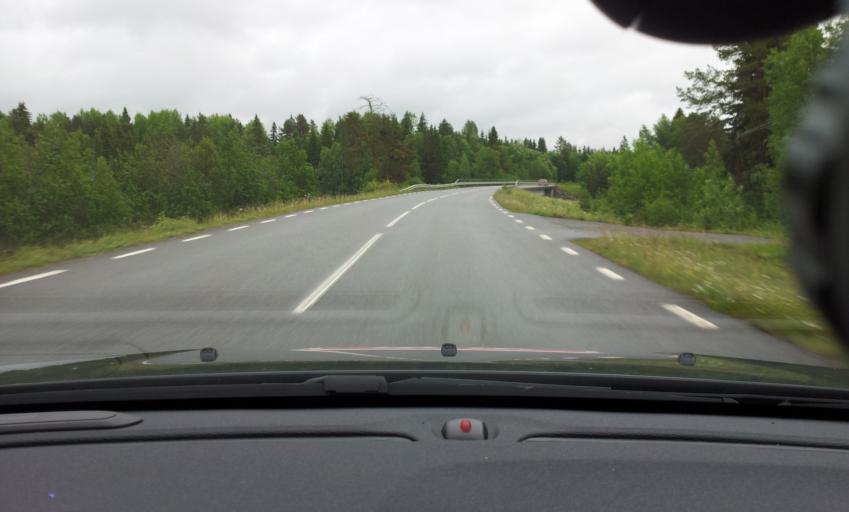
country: SE
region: Jaemtland
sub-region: Stroemsunds Kommun
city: Stroemsund
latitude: 63.5374
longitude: 15.4420
